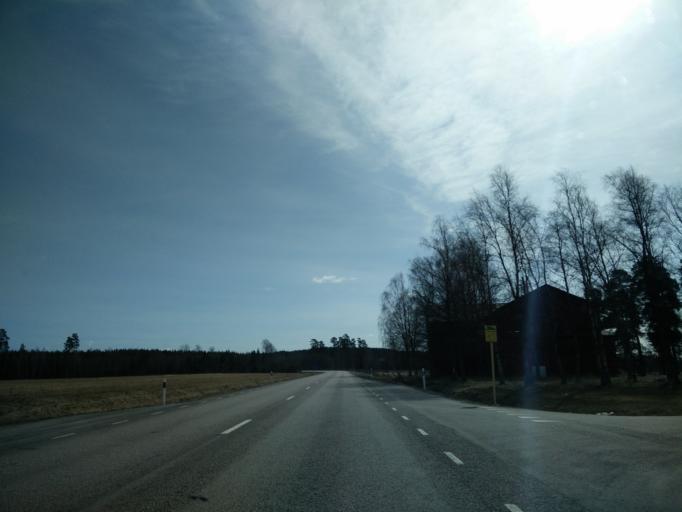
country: SE
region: Vaermland
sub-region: Hagfors Kommun
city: Hagfors
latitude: 60.0125
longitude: 13.6331
